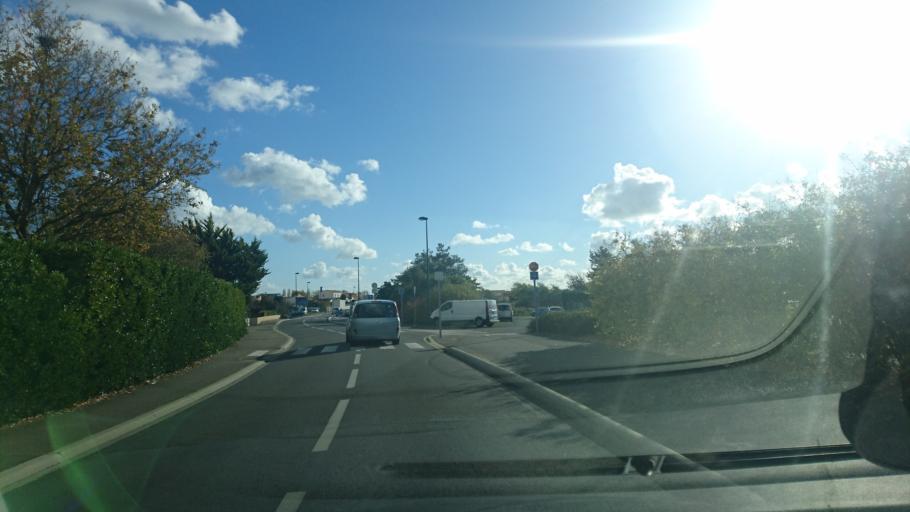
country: FR
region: Pays de la Loire
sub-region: Departement de la Vendee
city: Les Sables-d'Olonne
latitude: 46.5184
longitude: -1.7914
